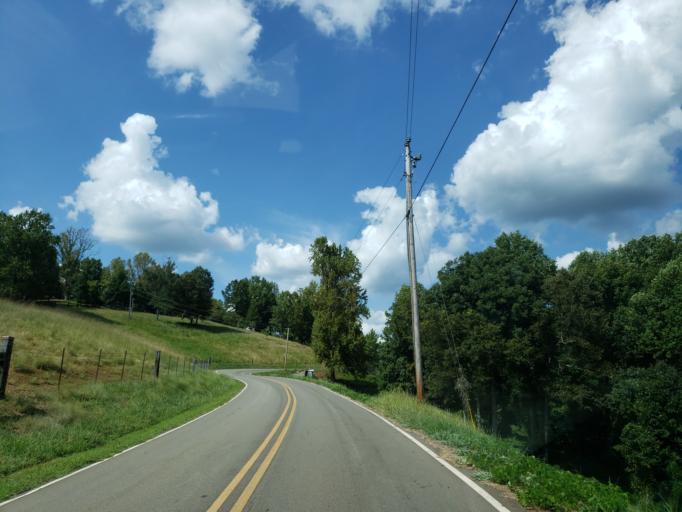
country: US
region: Georgia
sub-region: Pickens County
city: Jasper
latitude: 34.4171
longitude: -84.4480
